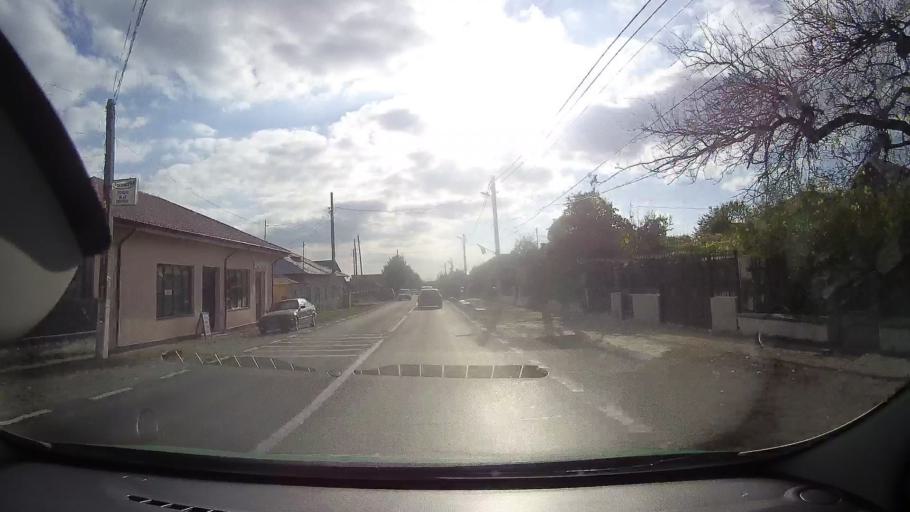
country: RO
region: Tulcea
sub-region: Comuna Topolog
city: Topolog
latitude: 44.8794
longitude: 28.3758
